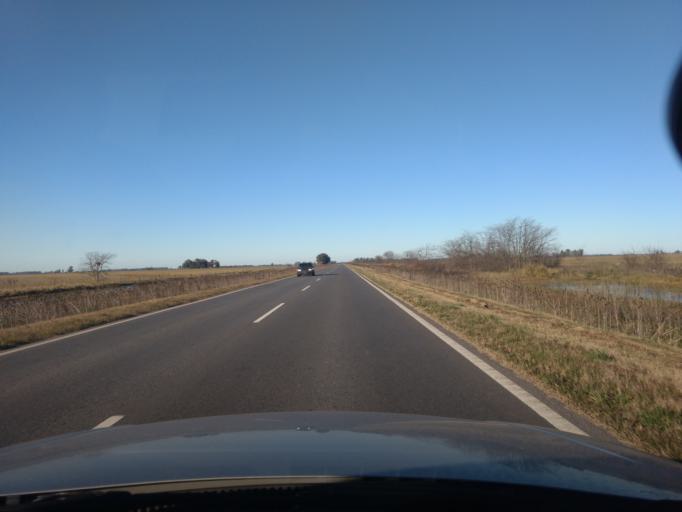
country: AR
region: Buenos Aires
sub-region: Partido de Navarro
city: Navarro
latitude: -34.8794
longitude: -59.2189
